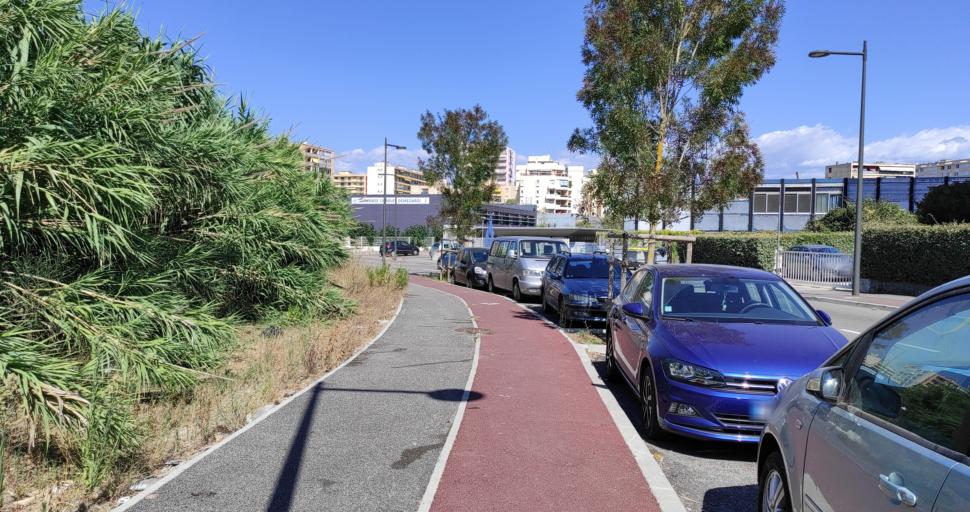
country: FR
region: Corsica
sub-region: Departement de la Corse-du-Sud
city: Ajaccio
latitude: 41.9355
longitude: 8.7369
